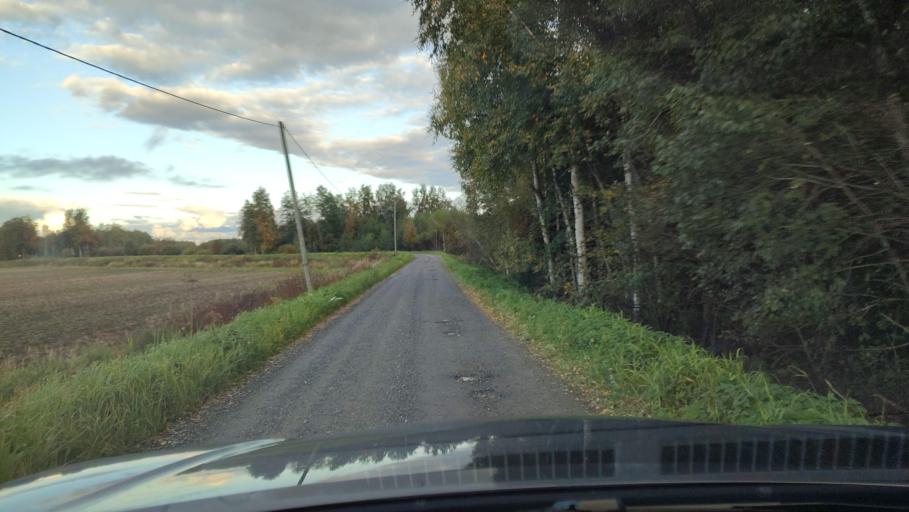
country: FI
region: Ostrobothnia
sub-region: Sydosterbotten
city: Kristinestad
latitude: 62.2314
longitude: 21.4461
